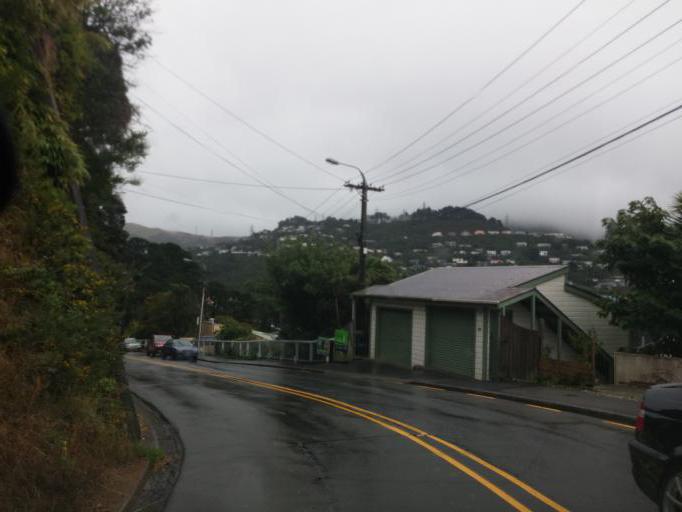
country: NZ
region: Wellington
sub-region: Wellington City
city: Kelburn
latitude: -41.2613
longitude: 174.7721
